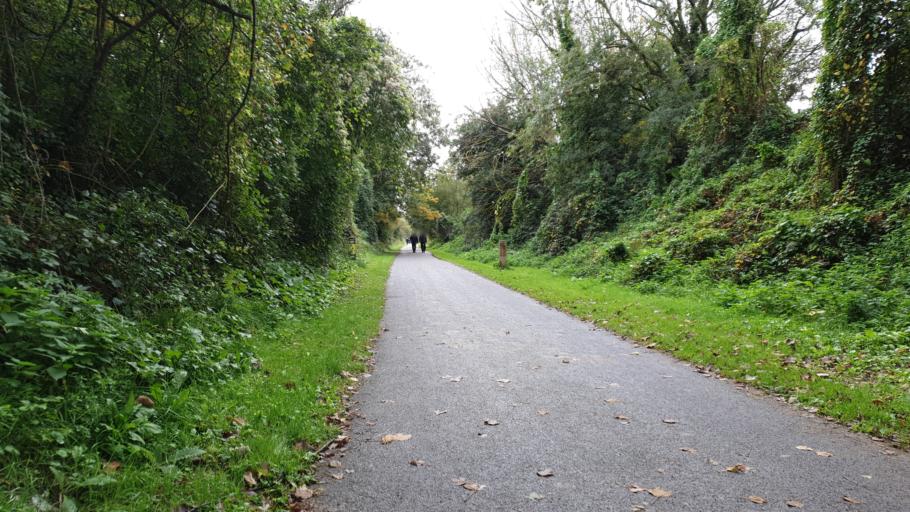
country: IE
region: Munster
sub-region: County Cork
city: Cork
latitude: 51.8942
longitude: -8.4160
